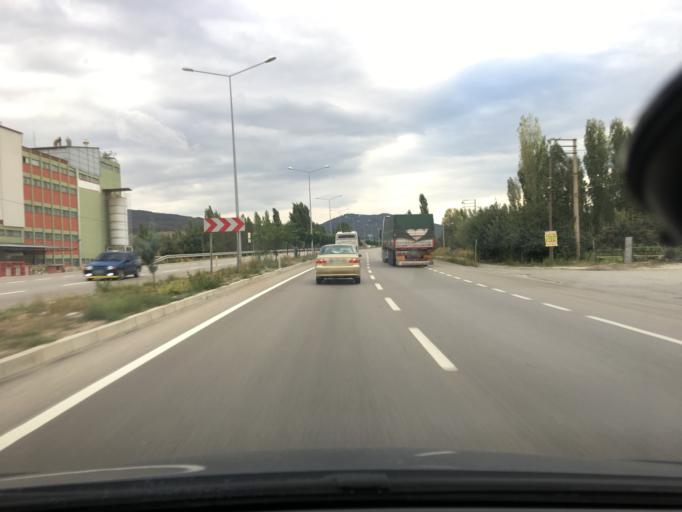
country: TR
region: Afyonkarahisar
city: Sincanli
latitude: 38.7277
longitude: 30.3437
